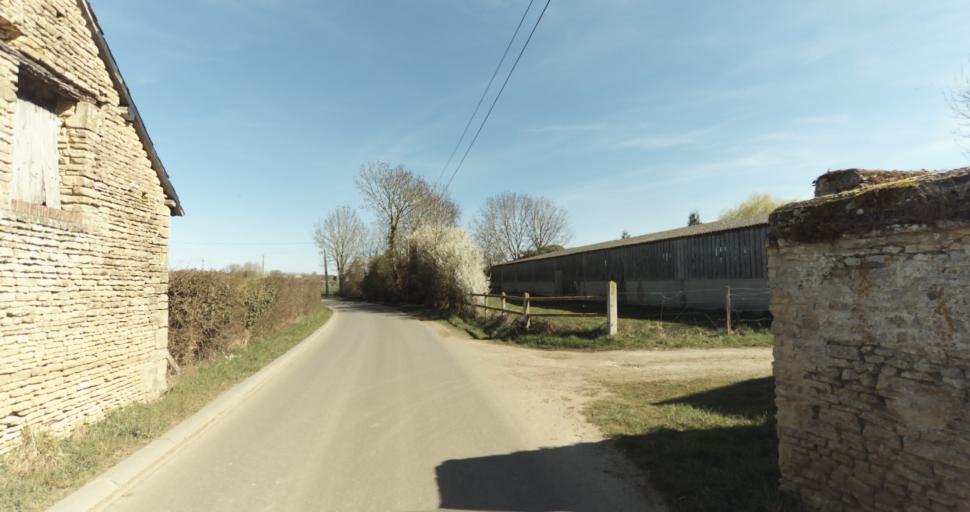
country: FR
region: Lower Normandy
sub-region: Departement du Calvados
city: Saint-Pierre-sur-Dives
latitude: 49.0500
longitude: -0.0331
